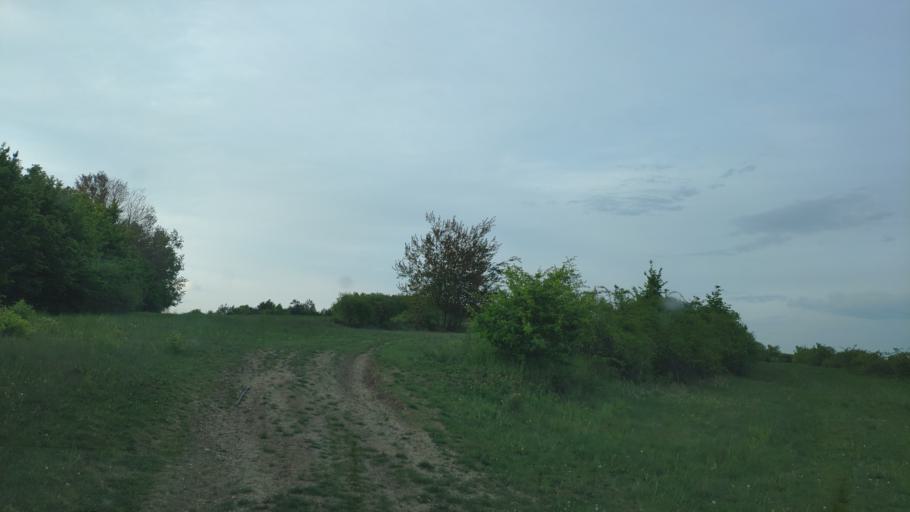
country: SK
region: Kosicky
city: Kosice
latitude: 48.7225
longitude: 21.3615
